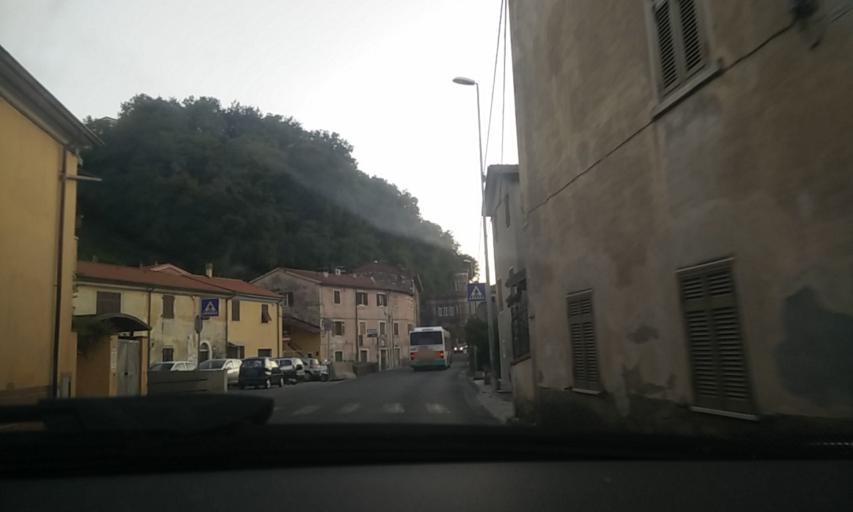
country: IT
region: Tuscany
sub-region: Provincia di Massa-Carrara
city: Carrara
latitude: 44.0677
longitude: 10.0857
